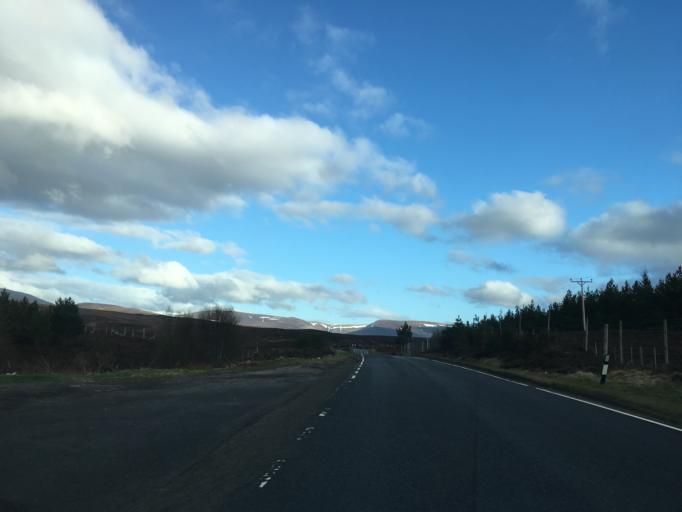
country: GB
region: Scotland
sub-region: Highland
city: Kingussie
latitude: 56.9858
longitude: -4.2413
